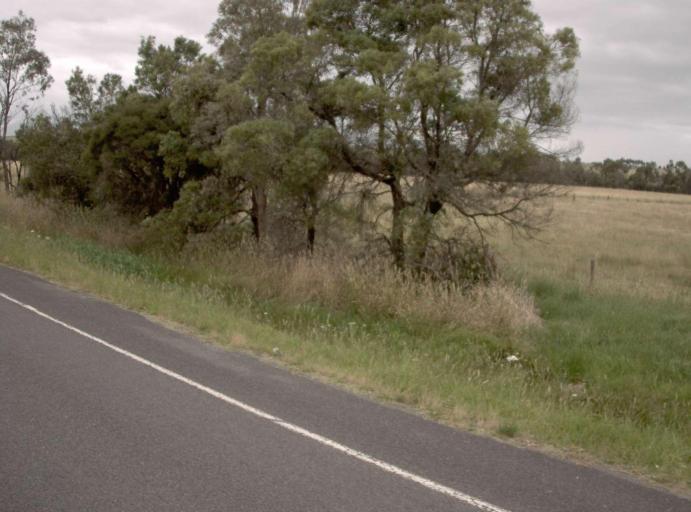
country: AU
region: Victoria
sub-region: Yarra Ranges
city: Yarra Glen
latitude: -37.6485
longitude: 145.3893
